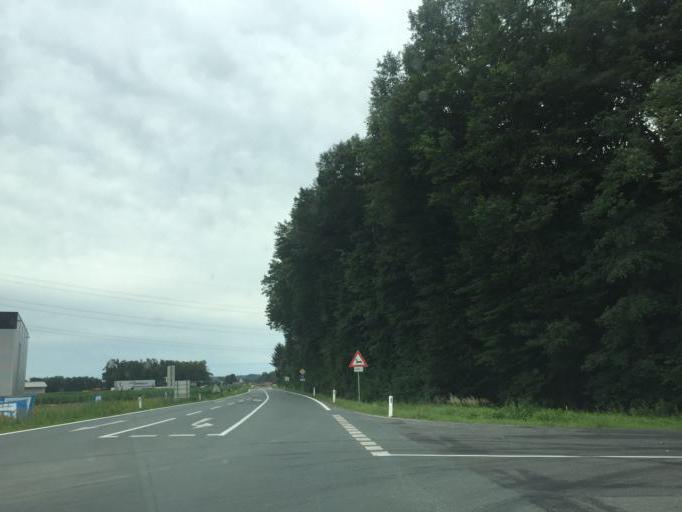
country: AT
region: Styria
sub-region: Politischer Bezirk Leibnitz
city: Spielfeld
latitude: 46.7214
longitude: 15.6509
